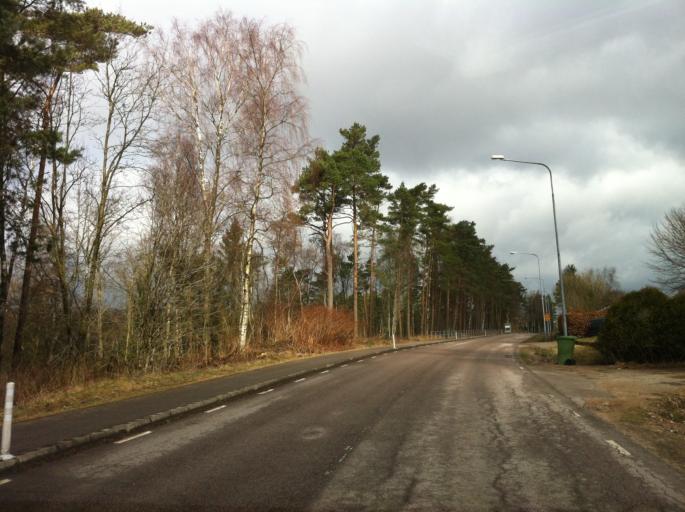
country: SE
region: Halland
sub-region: Halmstads Kommun
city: Oskarstrom
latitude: 56.8698
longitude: 13.0407
